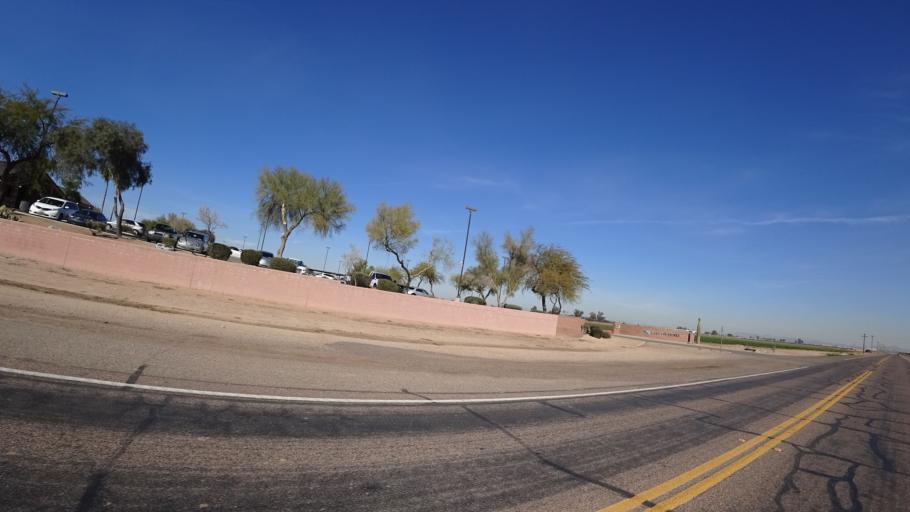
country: US
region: Arizona
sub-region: Maricopa County
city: Citrus Park
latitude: 33.5515
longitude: -112.3854
